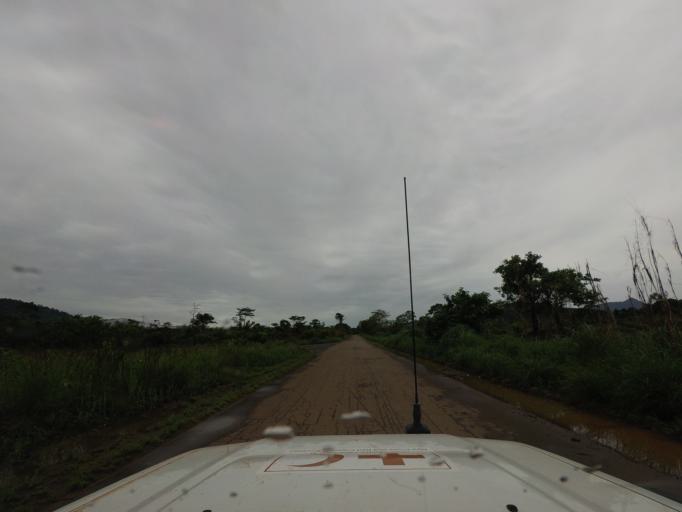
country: LR
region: Nimba
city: New Yekepa
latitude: 7.5651
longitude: -8.5467
